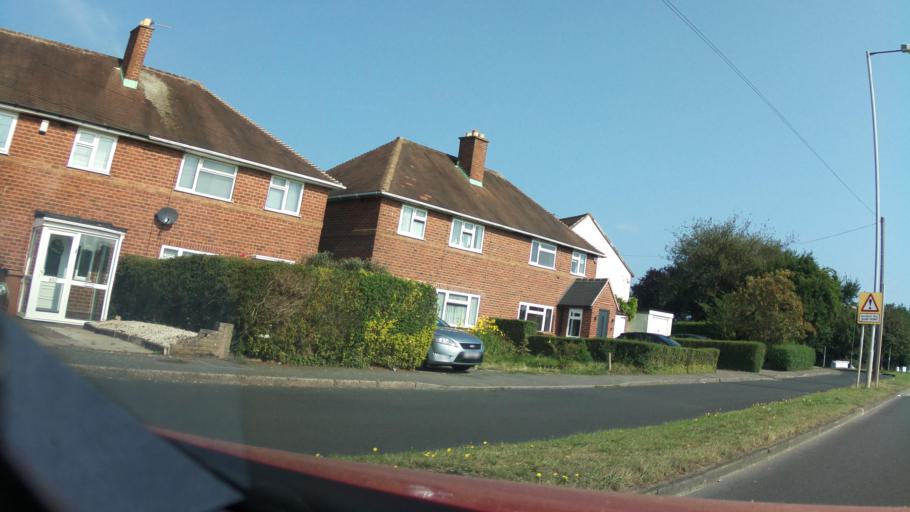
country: GB
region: England
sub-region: Walsall
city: Streetly
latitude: 52.5604
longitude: -1.8947
